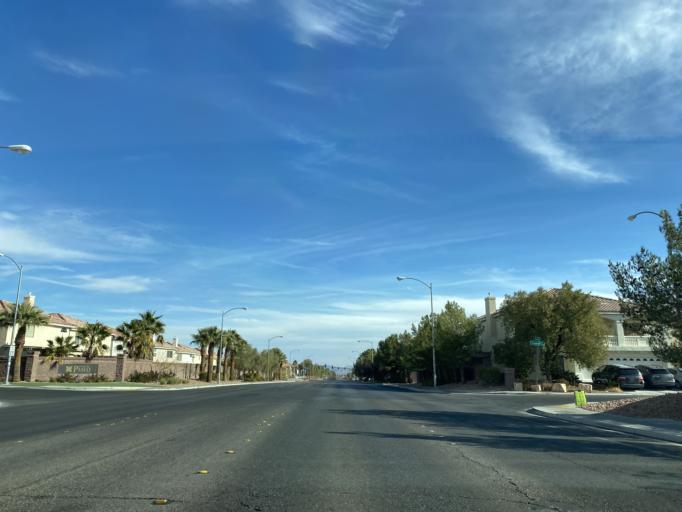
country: US
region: Nevada
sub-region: Clark County
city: Enterprise
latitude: 36.0491
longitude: -115.2286
